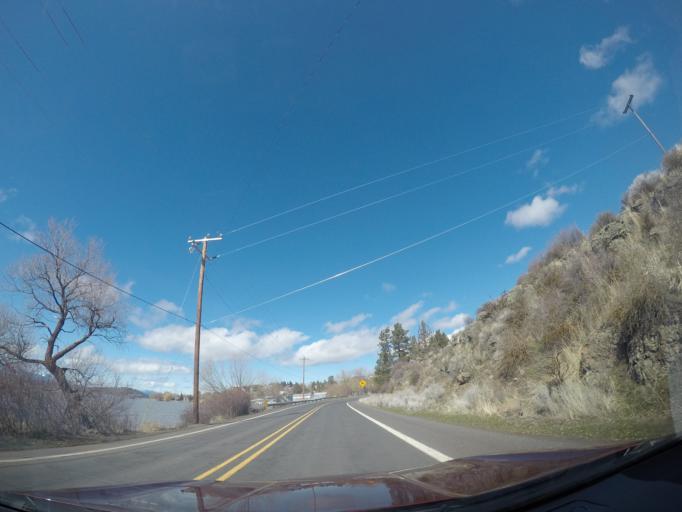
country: US
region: Oregon
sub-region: Klamath County
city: Klamath Falls
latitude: 42.2368
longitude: -121.8082
